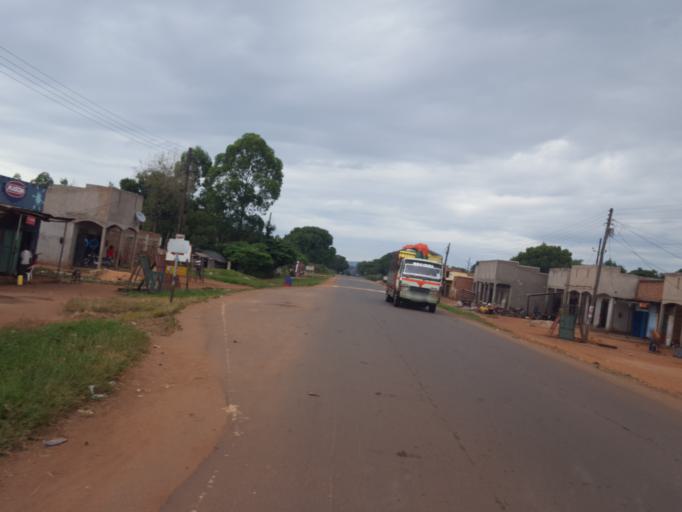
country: UG
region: Central Region
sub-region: Kiboga District
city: Kiboga
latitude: 1.0289
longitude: 31.6800
